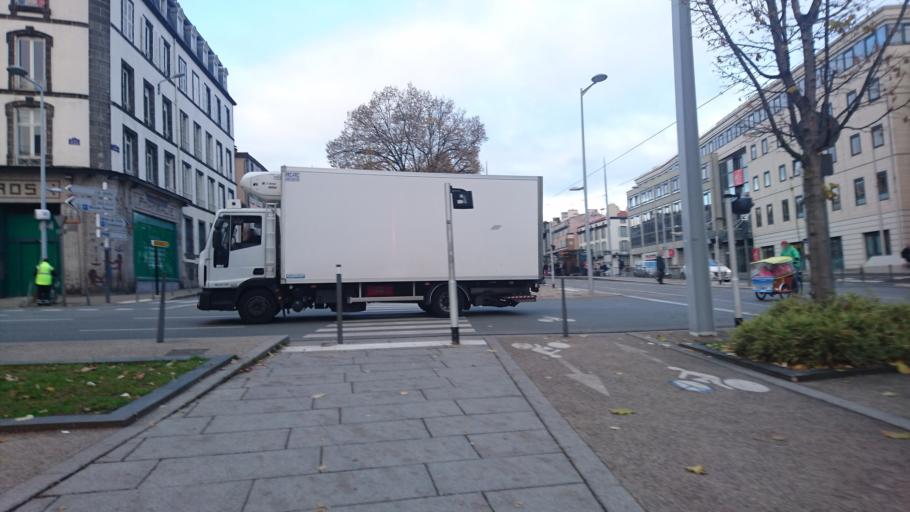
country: FR
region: Auvergne
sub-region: Departement du Puy-de-Dome
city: Clermont-Ferrand
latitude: 45.7810
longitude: 3.0913
